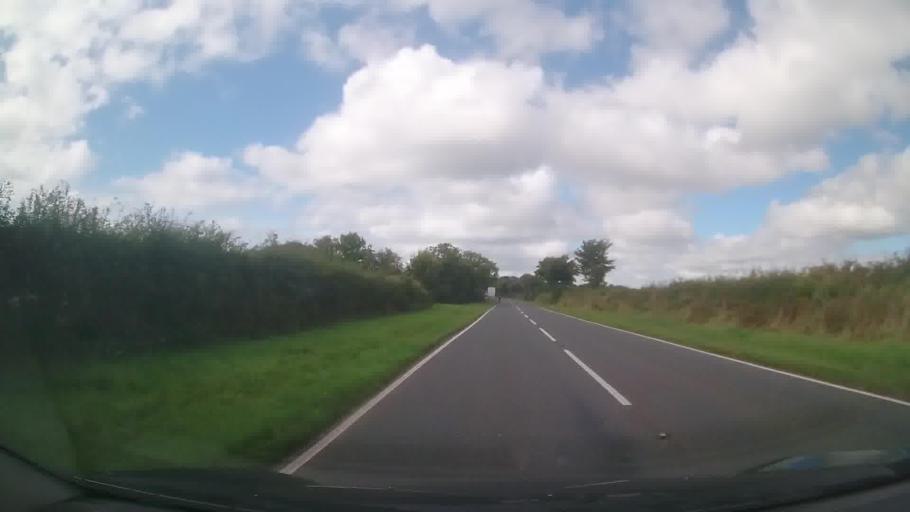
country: GB
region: Wales
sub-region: Pembrokeshire
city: Manorbier
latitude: 51.6518
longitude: -4.7762
